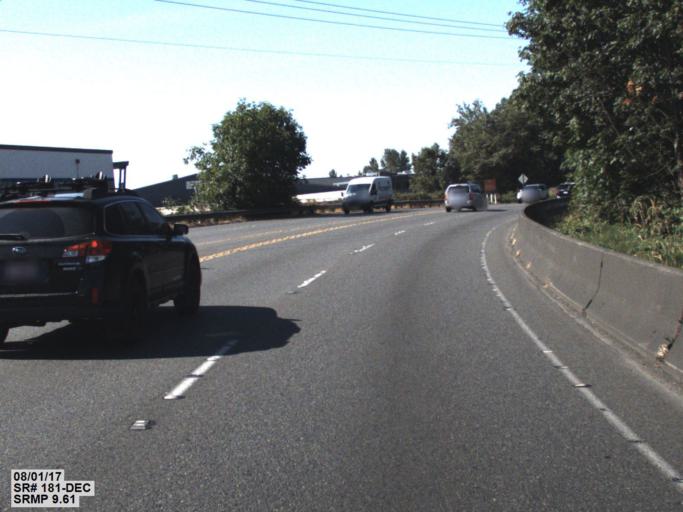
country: US
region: Washington
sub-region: King County
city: Tukwila
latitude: 47.4391
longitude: -122.2455
